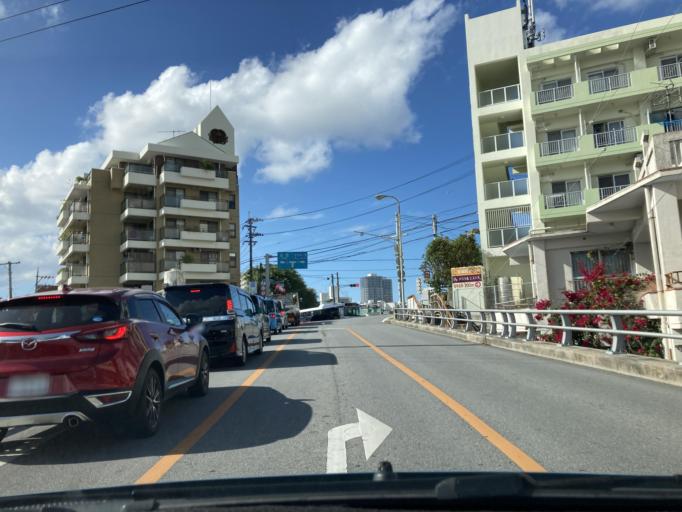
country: JP
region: Okinawa
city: Naha-shi
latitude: 26.2181
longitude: 127.7050
